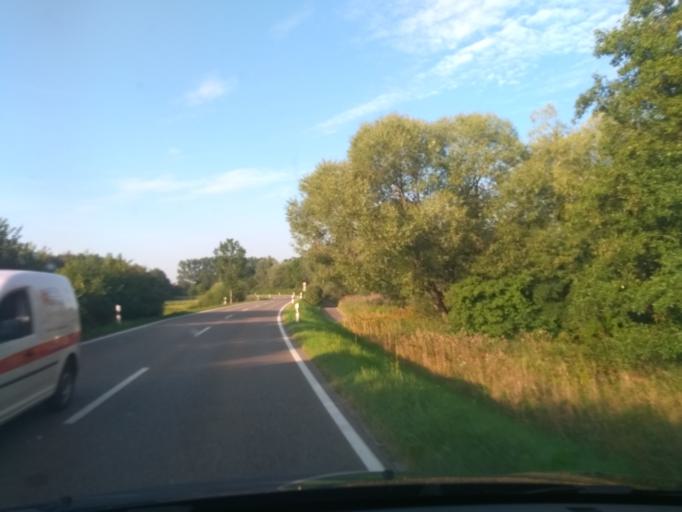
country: DE
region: Bavaria
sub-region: Upper Bavaria
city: Markt Indersdorf
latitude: 48.3635
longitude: 11.3798
